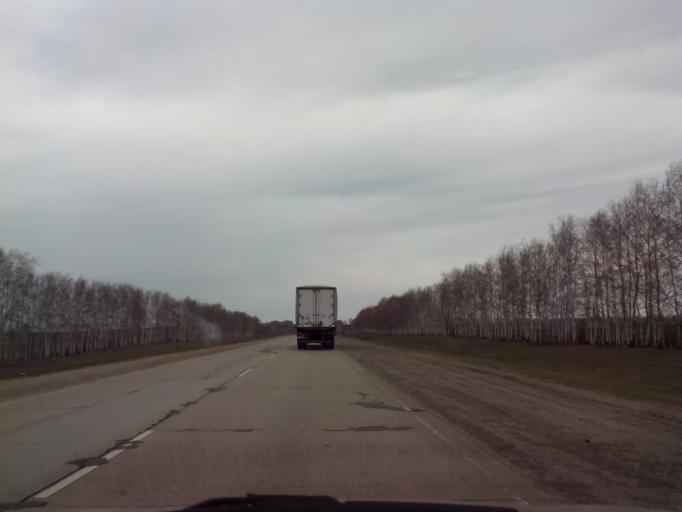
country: RU
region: Tambov
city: Pokrovo-Prigorodnoye
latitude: 52.6501
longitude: 41.3407
